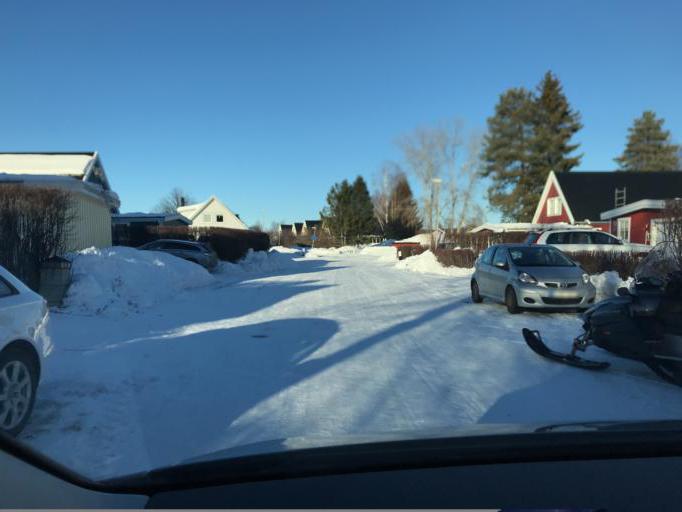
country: SE
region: Norrbotten
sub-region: Lulea Kommun
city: Sodra Sunderbyn
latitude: 65.6487
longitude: 21.9632
